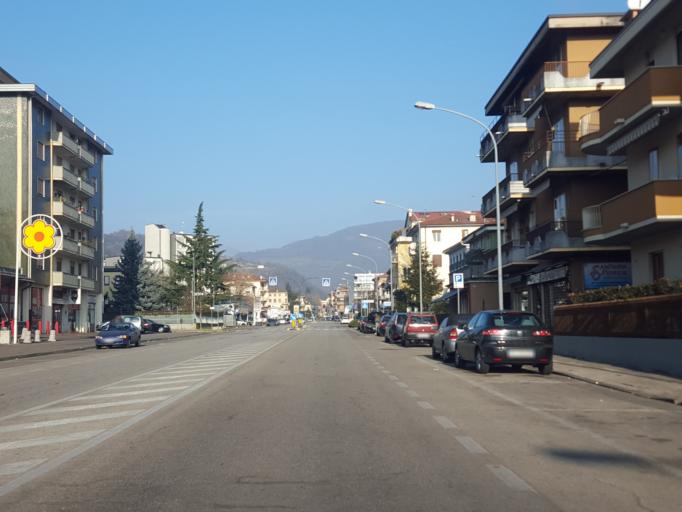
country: IT
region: Veneto
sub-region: Provincia di Vicenza
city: Valdagno
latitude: 45.6383
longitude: 11.3055
